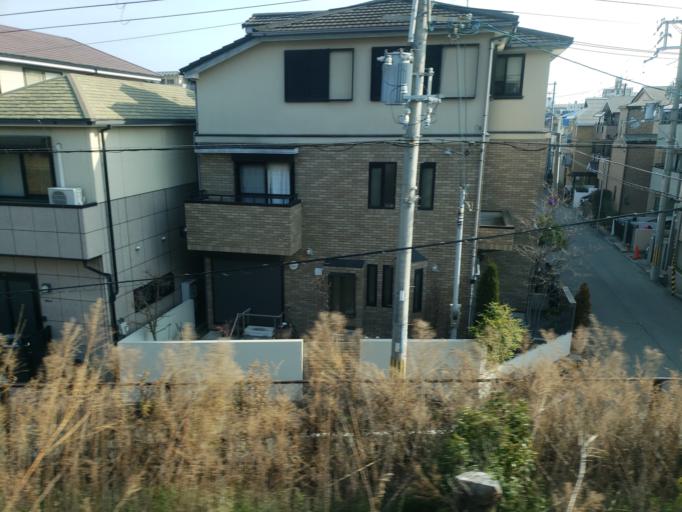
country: JP
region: Hyogo
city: Ashiya
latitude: 34.7250
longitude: 135.2722
